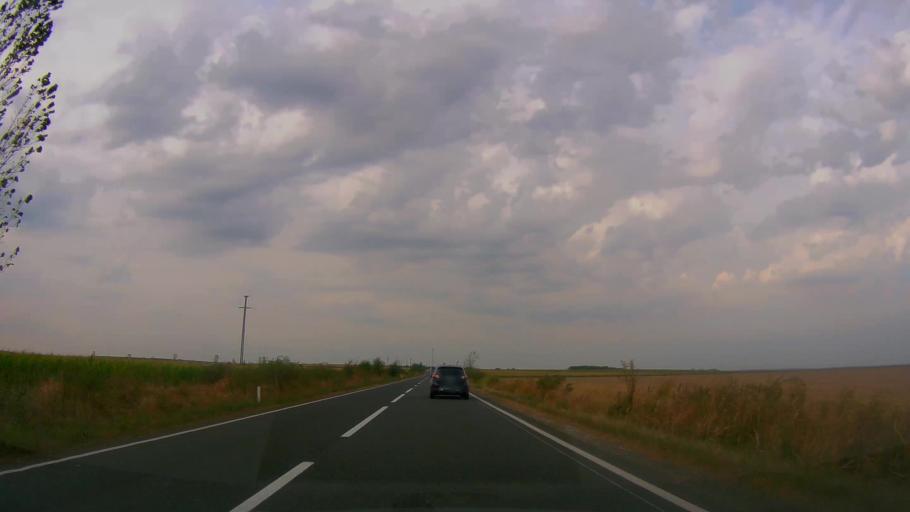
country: RO
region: Satu Mare
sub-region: Comuna Beltiug
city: Beltiug
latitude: 47.5649
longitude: 22.8642
